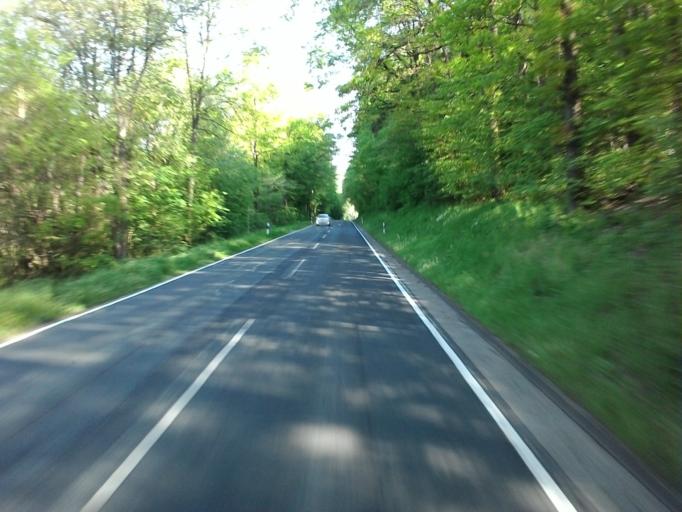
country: DE
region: Bavaria
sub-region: Regierungsbezirk Unterfranken
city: Marktheidenfeld
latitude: 49.8226
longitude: 9.5808
